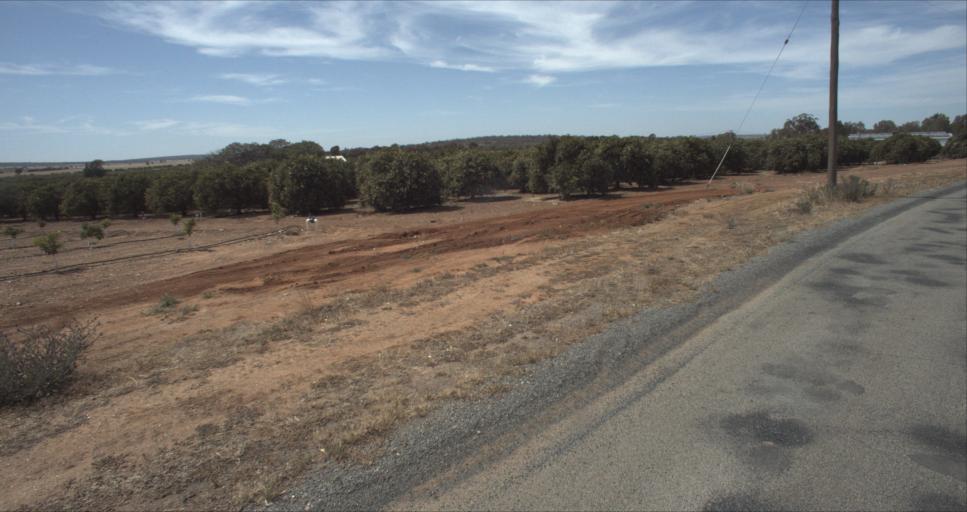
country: AU
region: New South Wales
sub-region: Leeton
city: Leeton
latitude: -34.5685
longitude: 146.4643
